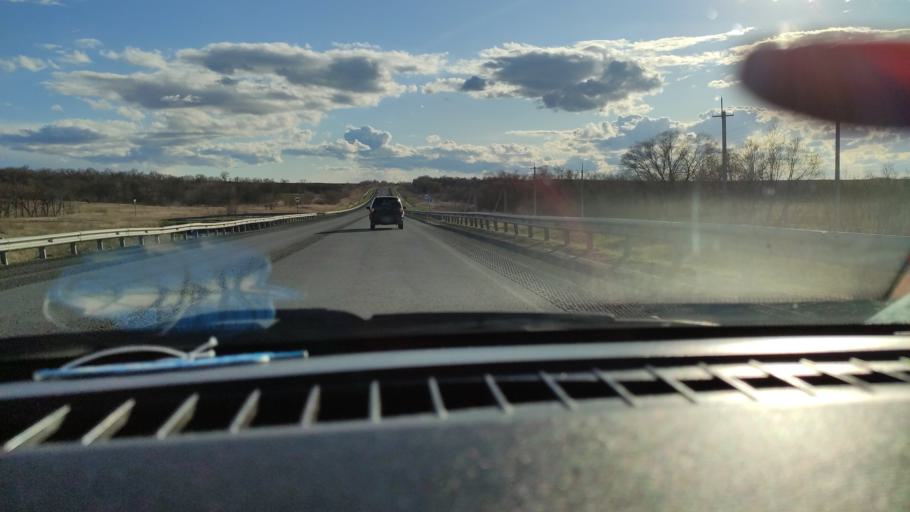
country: RU
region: Saratov
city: Shumeyka
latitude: 51.7778
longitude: 46.1168
